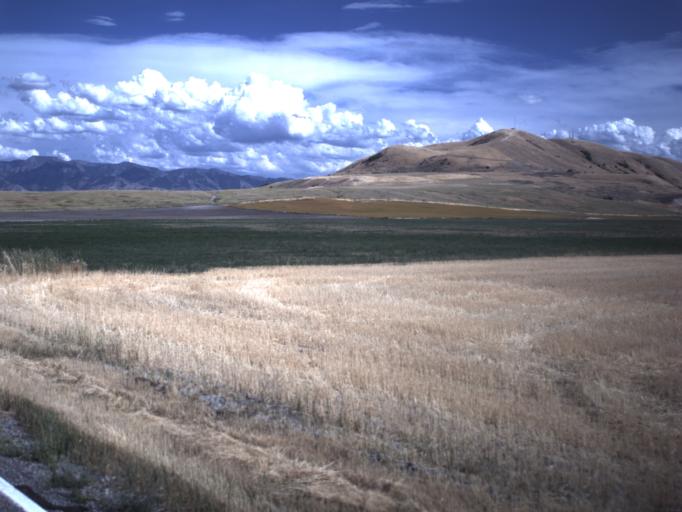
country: US
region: Utah
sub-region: Cache County
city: Benson
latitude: 41.9174
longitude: -111.9857
